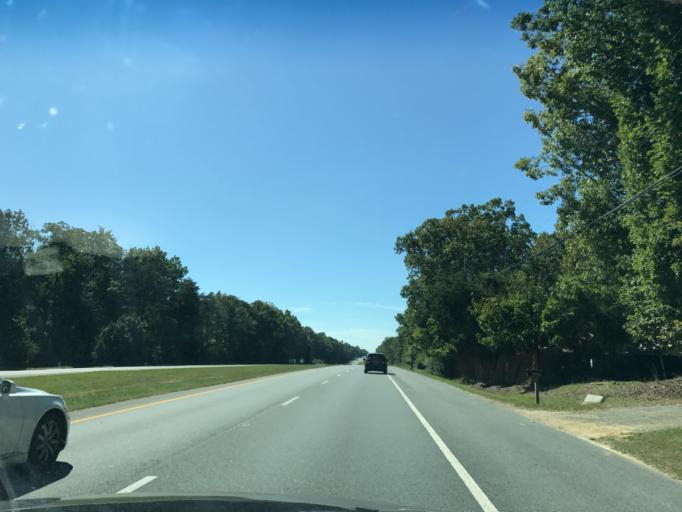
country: US
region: Maryland
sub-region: Charles County
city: La Plata
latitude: 38.4948
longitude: -76.9871
